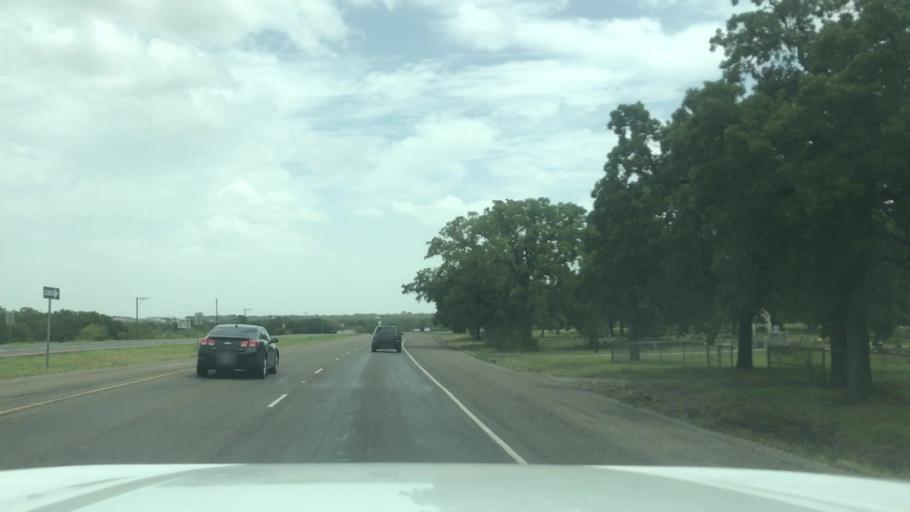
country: US
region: Texas
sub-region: McLennan County
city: Riesel
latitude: 31.4921
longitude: -96.9301
